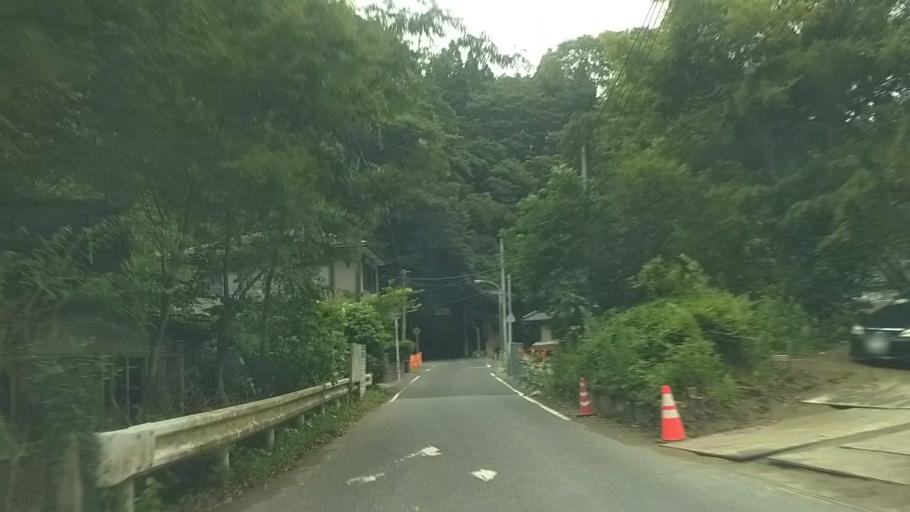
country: JP
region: Chiba
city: Kawaguchi
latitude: 35.2280
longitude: 140.1281
